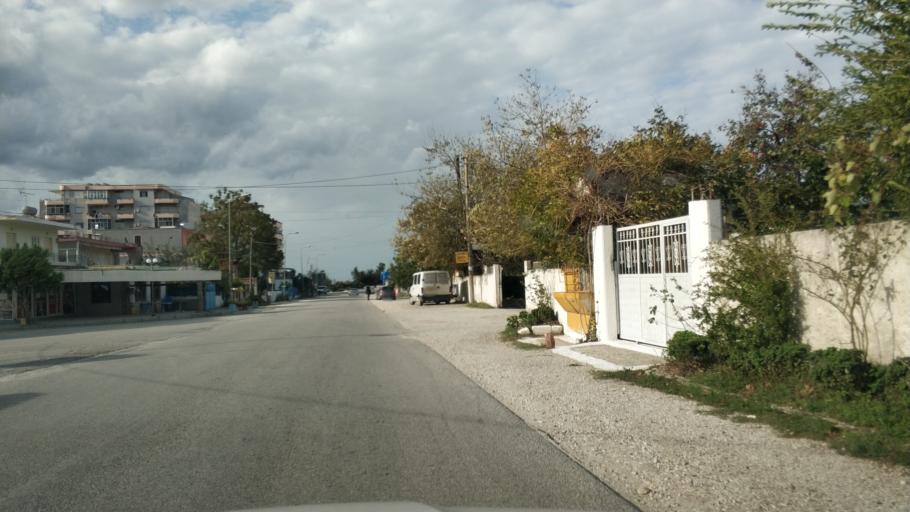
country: AL
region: Vlore
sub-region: Rrethi i Vlores
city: Orikum
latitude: 40.3299
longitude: 19.4775
